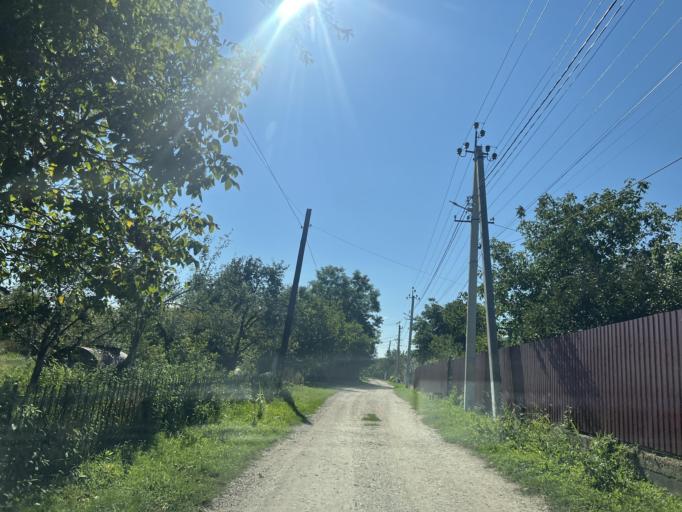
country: RO
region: Iasi
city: Ungheni-Prut
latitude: 47.1953
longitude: 27.7901
